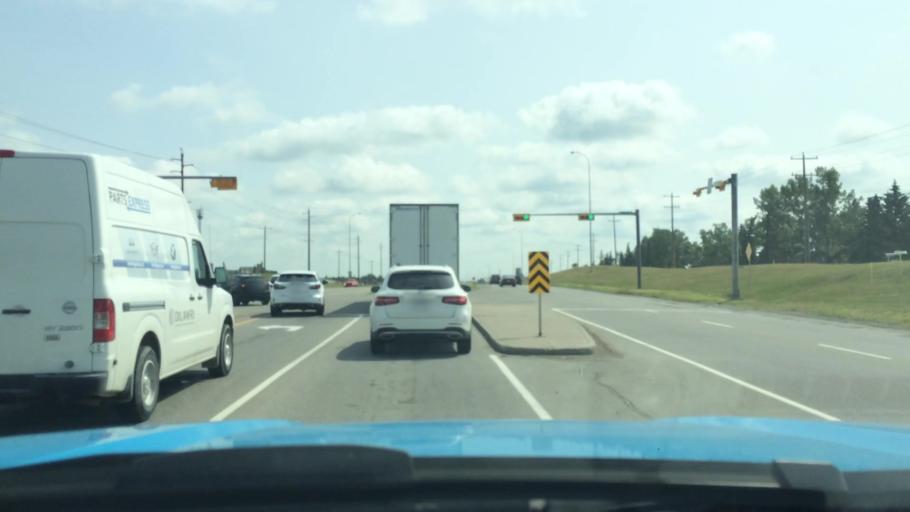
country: CA
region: Alberta
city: Calgary
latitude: 51.0960
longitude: -113.9667
